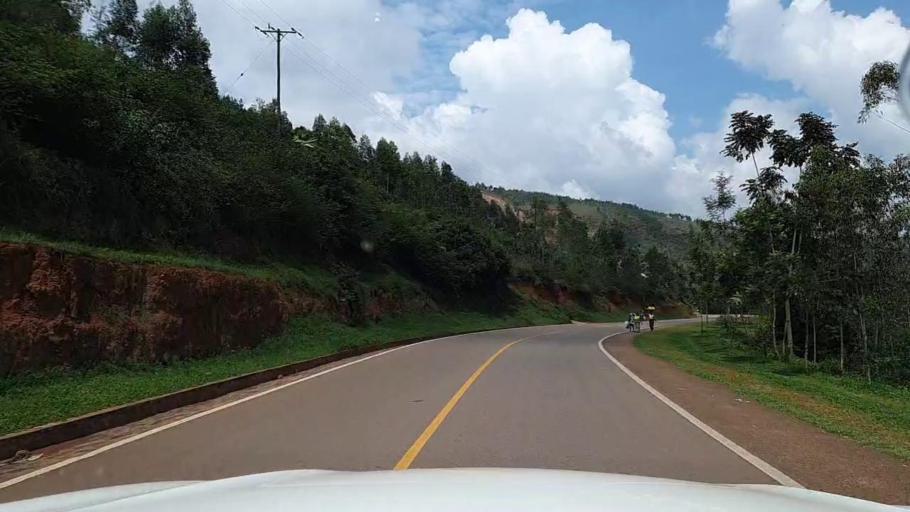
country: RW
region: Kigali
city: Kigali
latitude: -1.8376
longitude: 30.0819
